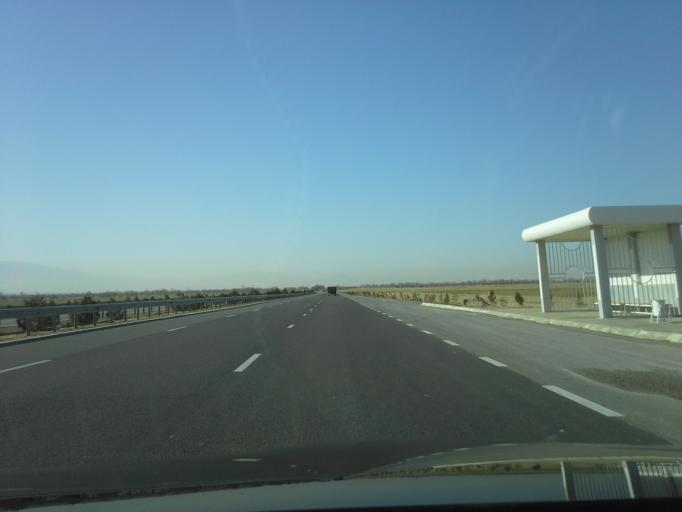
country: TM
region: Ahal
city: Annau
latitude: 37.8968
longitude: 58.5965
